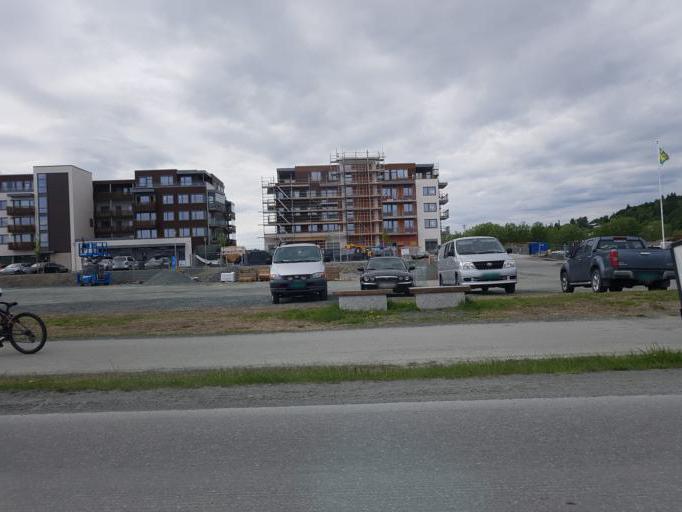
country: NO
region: Nord-Trondelag
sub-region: Levanger
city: Levanger
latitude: 63.7372
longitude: 11.2815
